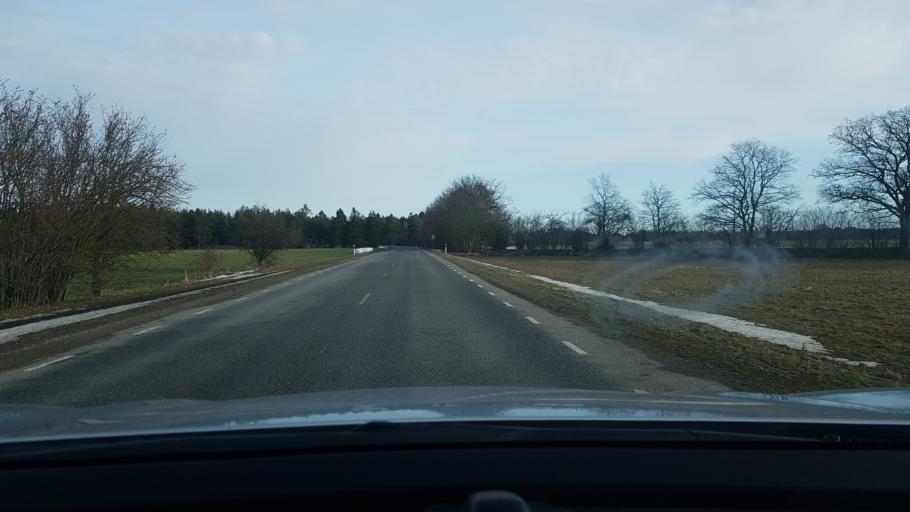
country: EE
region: Saare
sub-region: Kuressaare linn
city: Kuressaare
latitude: 58.4073
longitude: 22.6508
